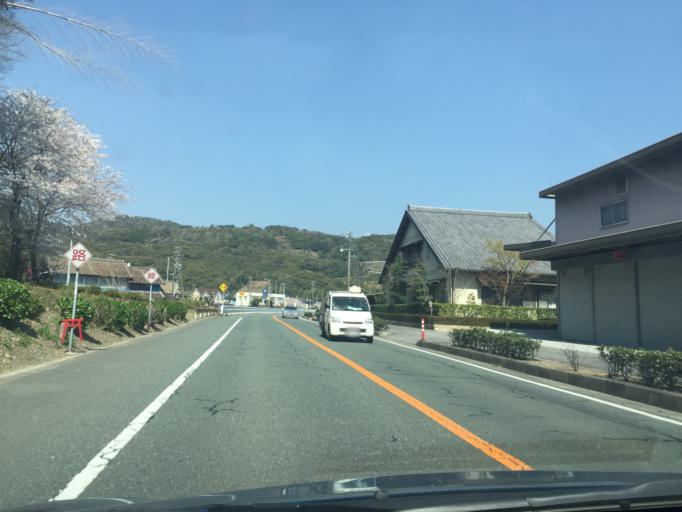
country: JP
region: Shizuoka
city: Kosai-shi
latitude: 34.7995
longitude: 137.6189
